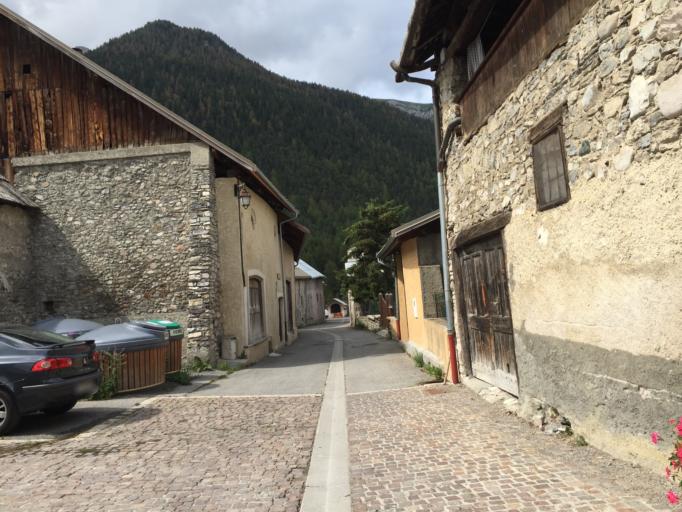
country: FR
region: Provence-Alpes-Cote d'Azur
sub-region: Departement des Hautes-Alpes
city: Guillestre
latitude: 44.6673
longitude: 6.7763
